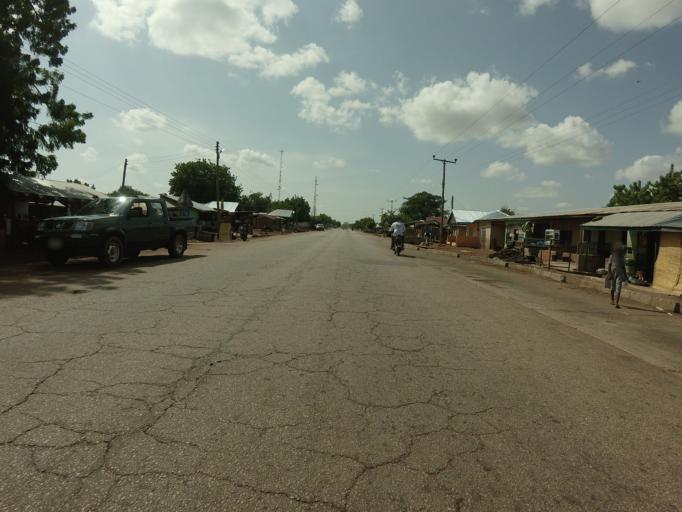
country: GH
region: Northern
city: Savelugu
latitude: 9.8685
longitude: -0.8713
